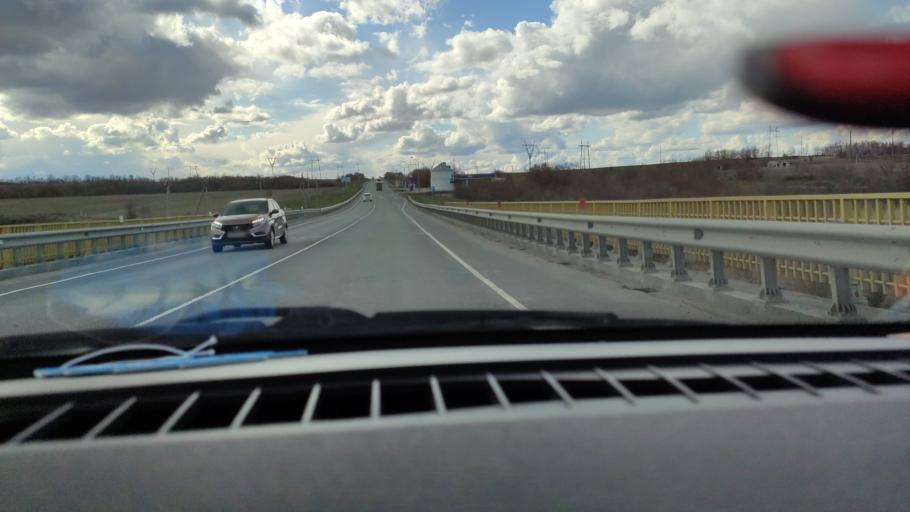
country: RU
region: Saratov
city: Tersa
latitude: 52.0990
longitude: 47.5228
